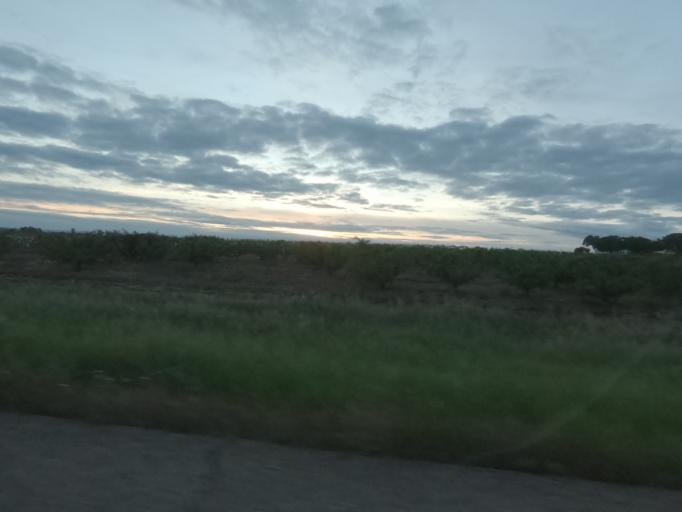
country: ES
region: Extremadura
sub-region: Provincia de Badajoz
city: Badajoz
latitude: 38.9406
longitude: -6.9201
